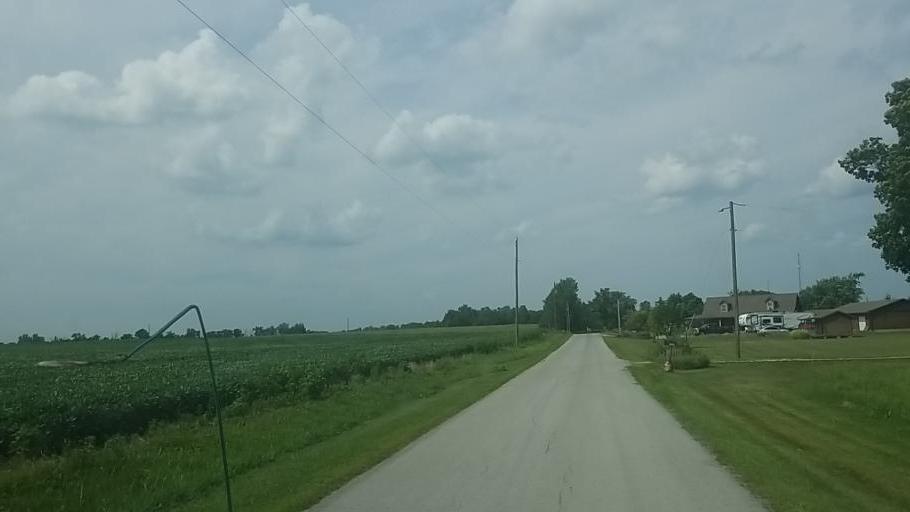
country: US
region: Ohio
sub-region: Hardin County
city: Forest
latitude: 40.8153
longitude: -83.4674
